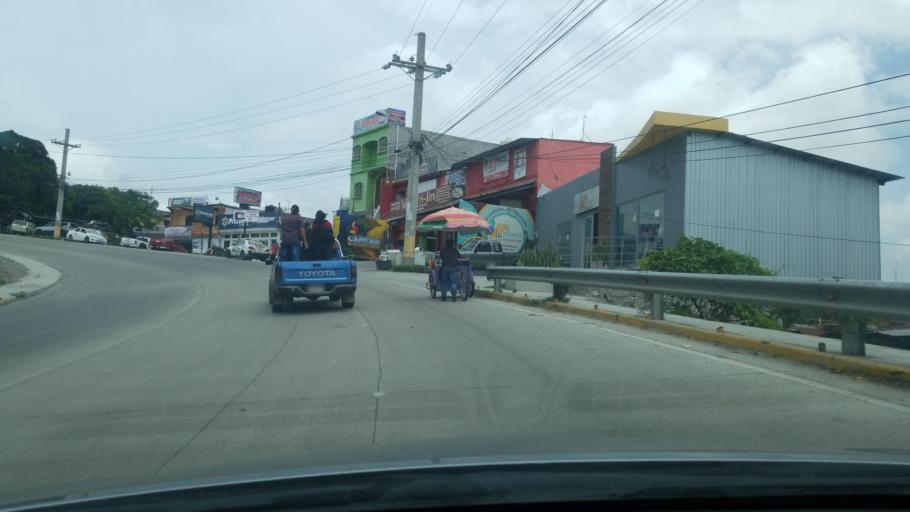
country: HN
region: Copan
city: Santa Rosa de Copan
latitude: 14.7682
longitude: -88.7727
